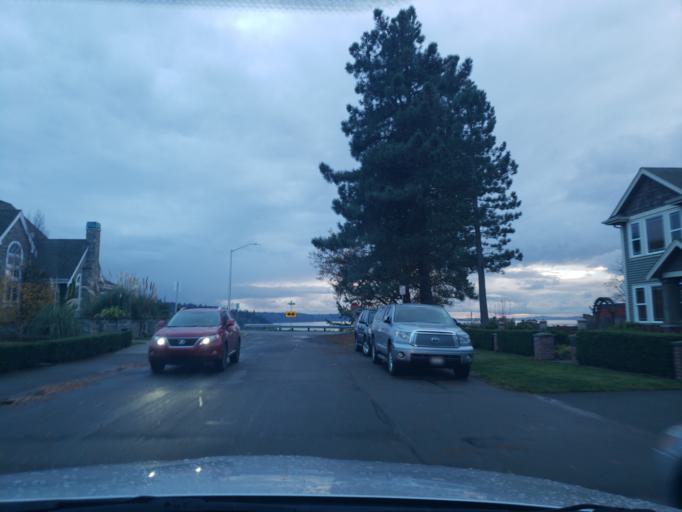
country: US
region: Washington
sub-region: Snohomish County
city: Woodway
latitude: 47.7675
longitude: -122.3840
